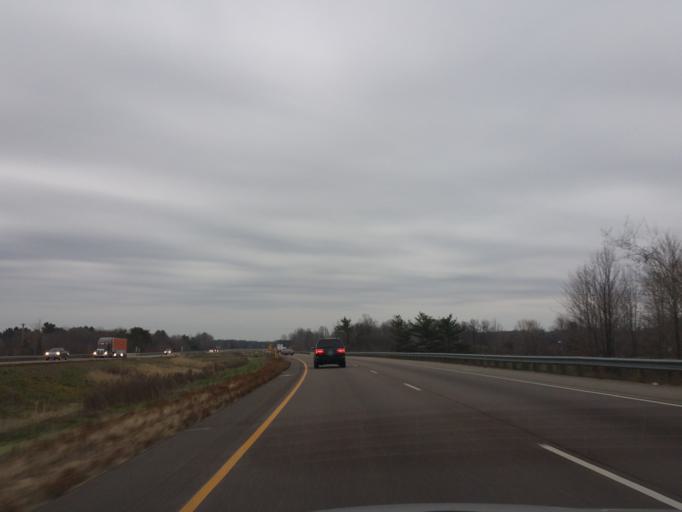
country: US
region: Wisconsin
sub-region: Dunn County
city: Menomonie
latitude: 44.9145
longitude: -91.9943
